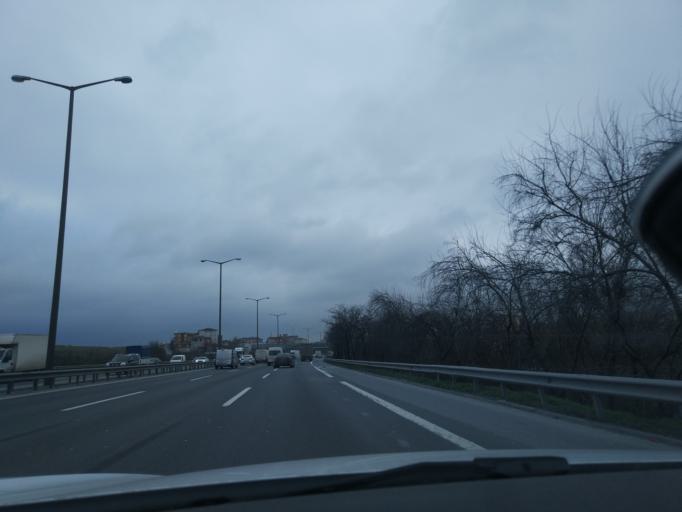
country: TR
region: Istanbul
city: Esenyurt
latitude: 41.0580
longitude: 28.7324
